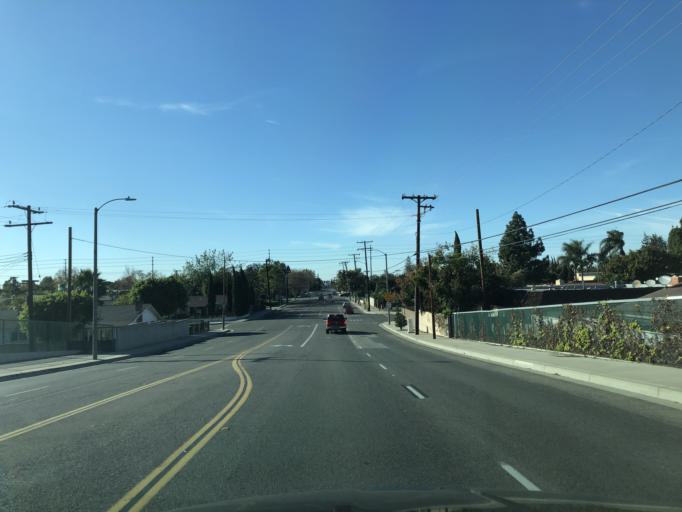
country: US
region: California
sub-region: Orange County
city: Orange
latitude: 33.7732
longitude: -117.8336
